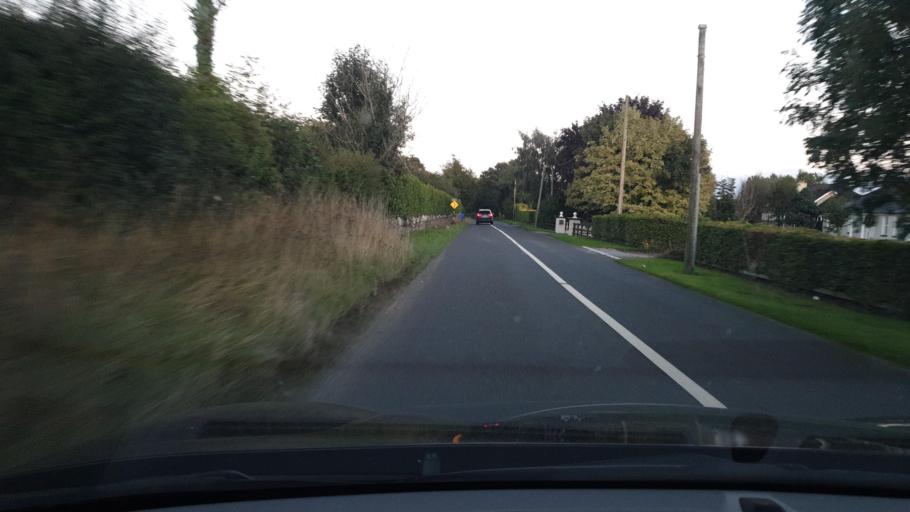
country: IE
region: Leinster
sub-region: Kildare
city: Prosperous
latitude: 53.3427
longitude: -6.7269
